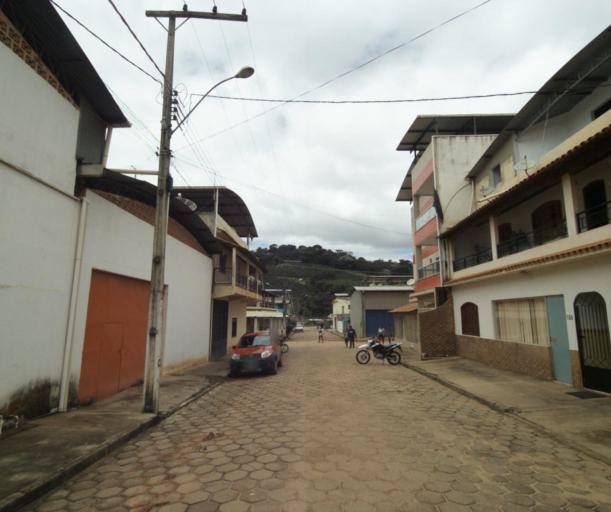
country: BR
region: Espirito Santo
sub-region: Irupi
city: Irupi
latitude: -20.3496
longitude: -41.6373
